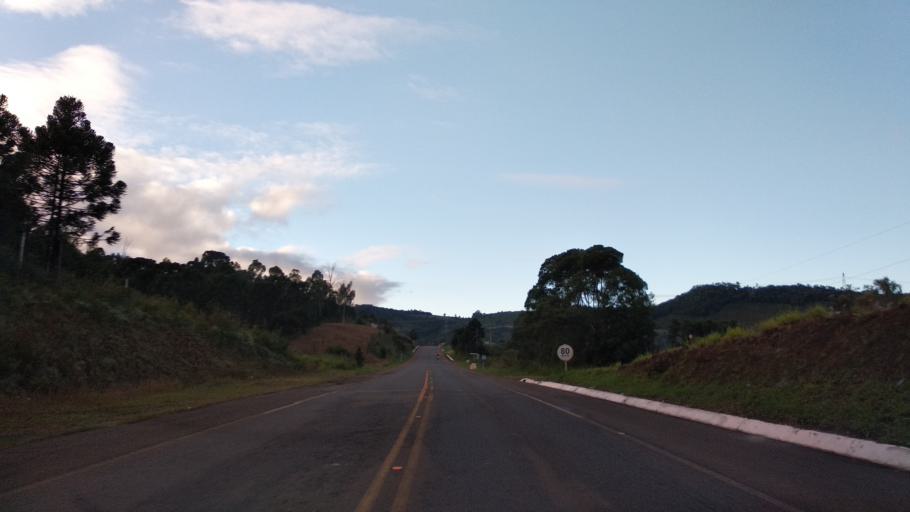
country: BR
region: Santa Catarina
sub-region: Curitibanos
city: Curitibanos
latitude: -27.5532
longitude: -50.8450
